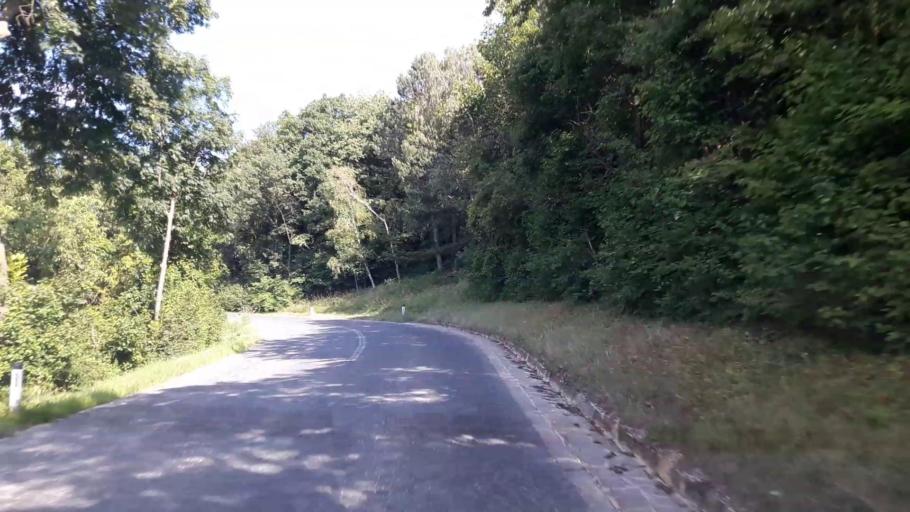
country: AT
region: Lower Austria
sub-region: Politischer Bezirk Wien-Umgebung
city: Klosterneuburg
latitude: 48.2861
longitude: 16.3246
